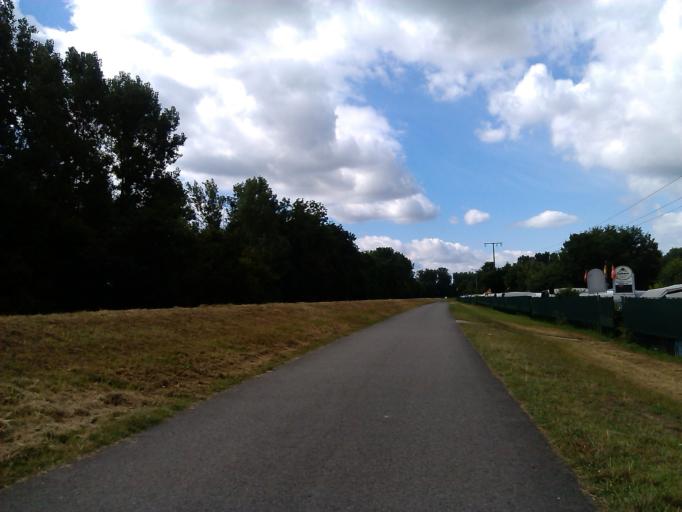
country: DE
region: Rheinland-Pfalz
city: Altrip
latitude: 49.4038
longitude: 8.4877
